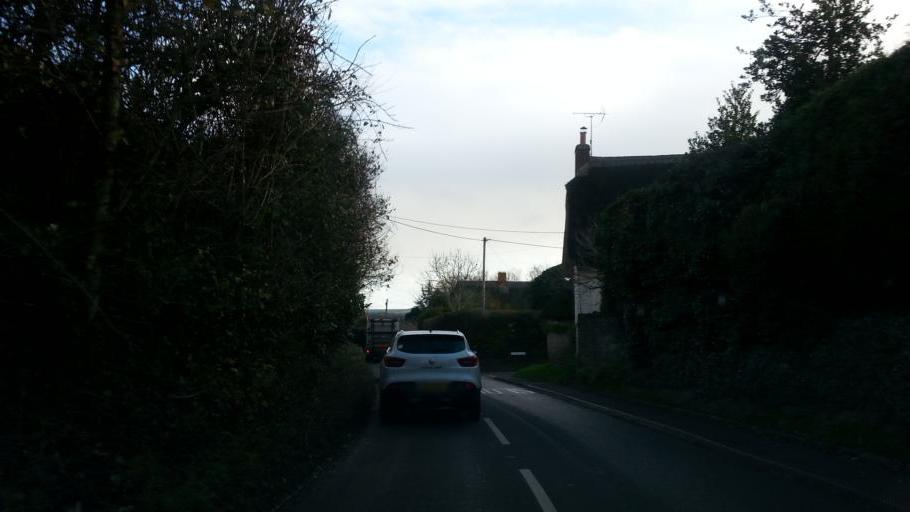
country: GB
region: England
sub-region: Oxfordshire
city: Faringdon
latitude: 51.6256
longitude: -1.5785
